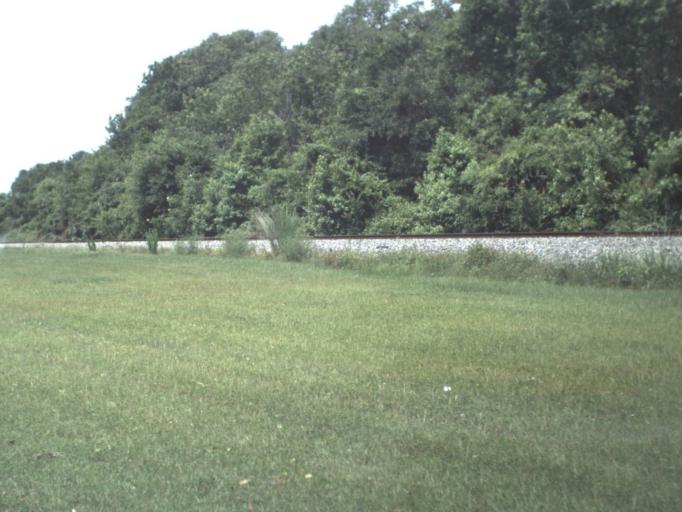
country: US
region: Florida
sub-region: Nassau County
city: Fernandina Beach
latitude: 30.6369
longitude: -81.4588
